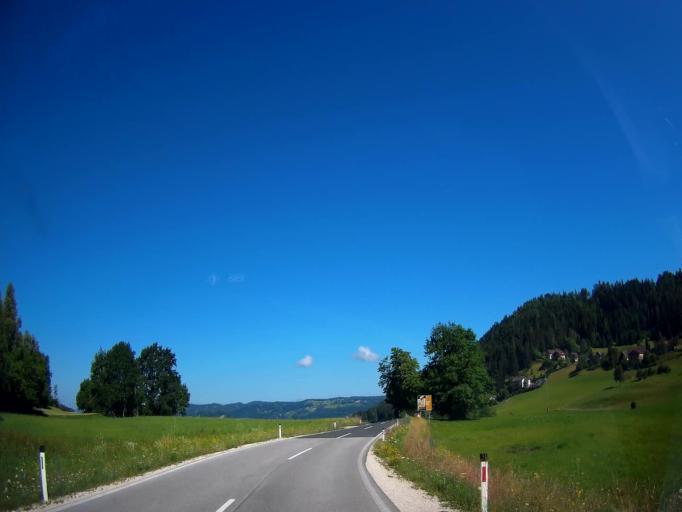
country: AT
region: Carinthia
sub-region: Politischer Bezirk Klagenfurt Land
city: Grafenstein
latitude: 46.5364
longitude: 14.4511
